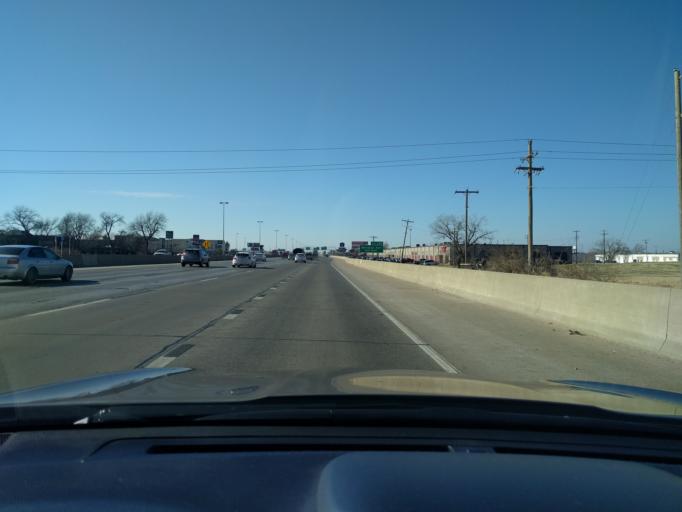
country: US
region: Oklahoma
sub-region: Oklahoma County
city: Warr Acres
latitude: 35.4603
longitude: -97.5919
